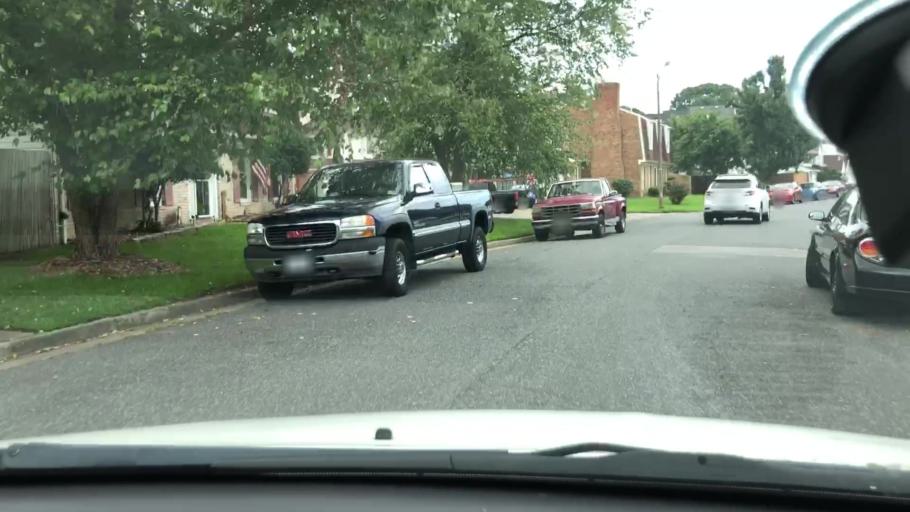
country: US
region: Virginia
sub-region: City of Virginia Beach
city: Virginia Beach
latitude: 36.8453
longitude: -76.1179
